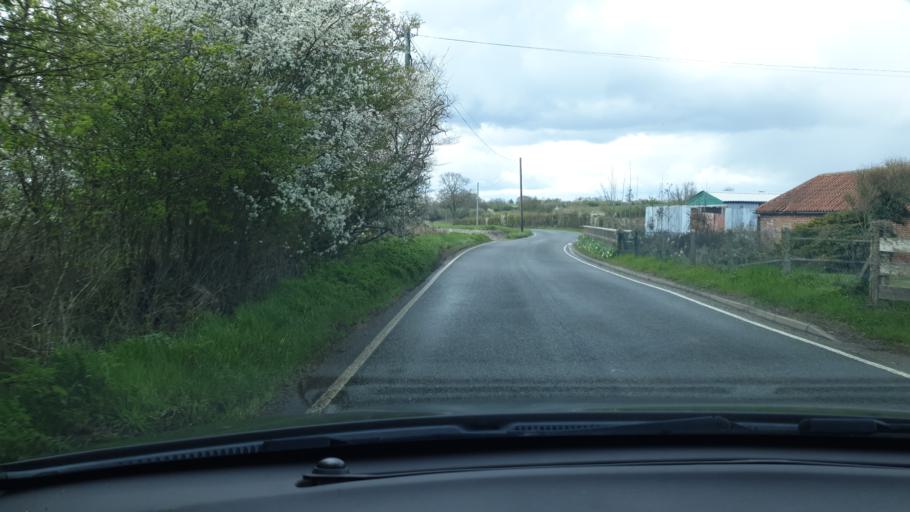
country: GB
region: England
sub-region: Essex
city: Little Clacton
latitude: 51.9088
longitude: 1.1701
